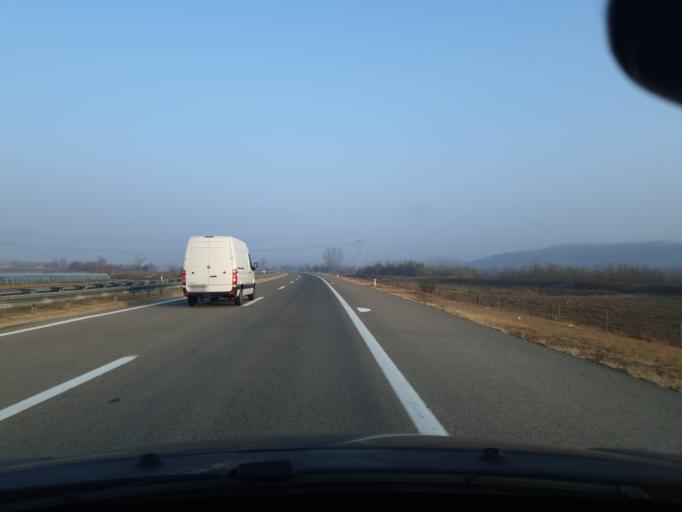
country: RS
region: Central Serbia
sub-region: Jablanicki Okrug
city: Leskovac
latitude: 43.0068
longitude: 22.0248
